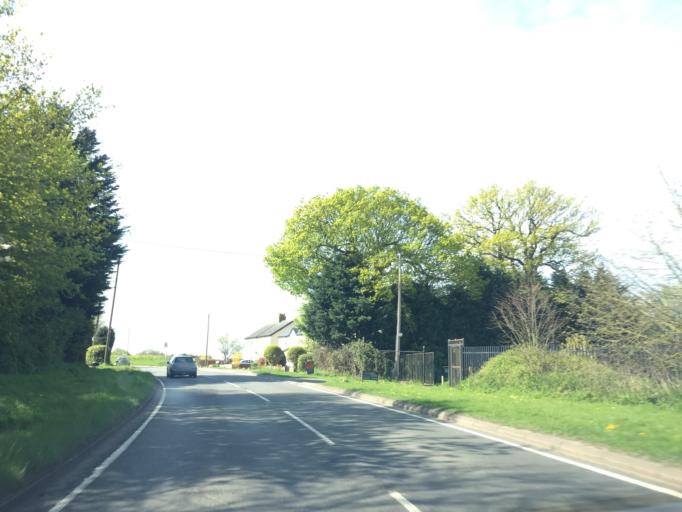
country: GB
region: England
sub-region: Greater London
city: Collier Row
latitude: 51.6460
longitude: 0.1659
